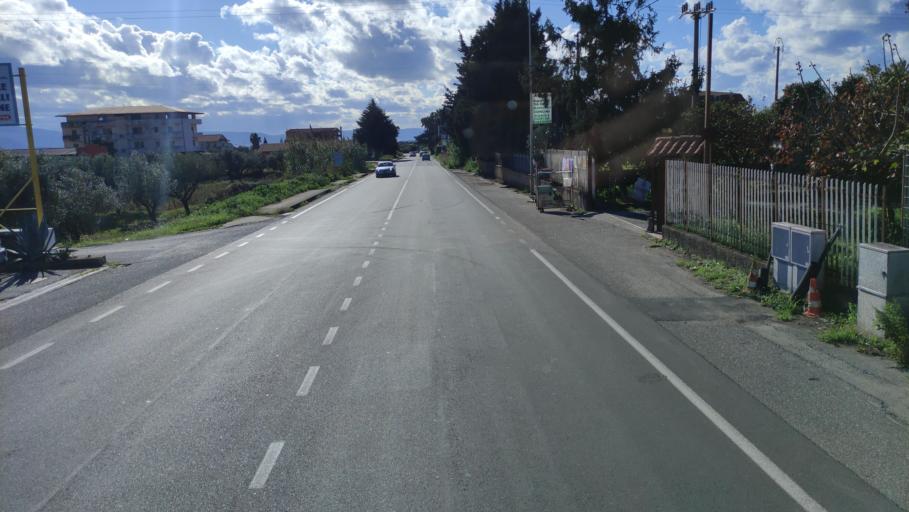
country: IT
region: Calabria
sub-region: Provincia di Catanzaro
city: Nicastro-Sambiase
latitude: 38.9330
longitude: 16.2873
